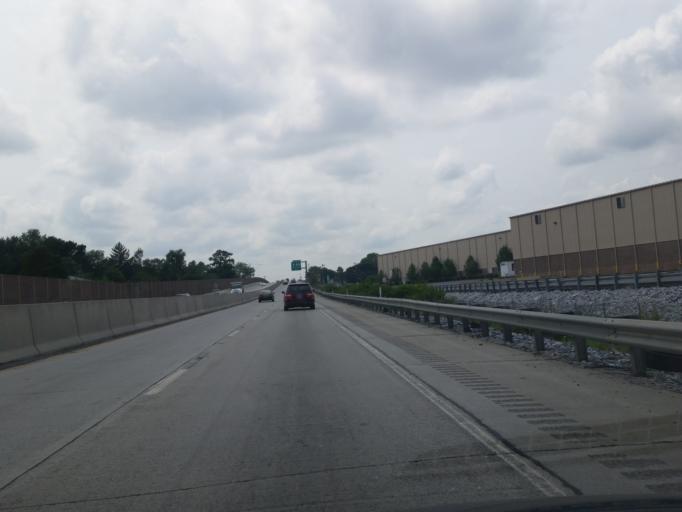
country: US
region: Pennsylvania
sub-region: Cumberland County
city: Lower Allen
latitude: 40.2356
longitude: -76.9039
